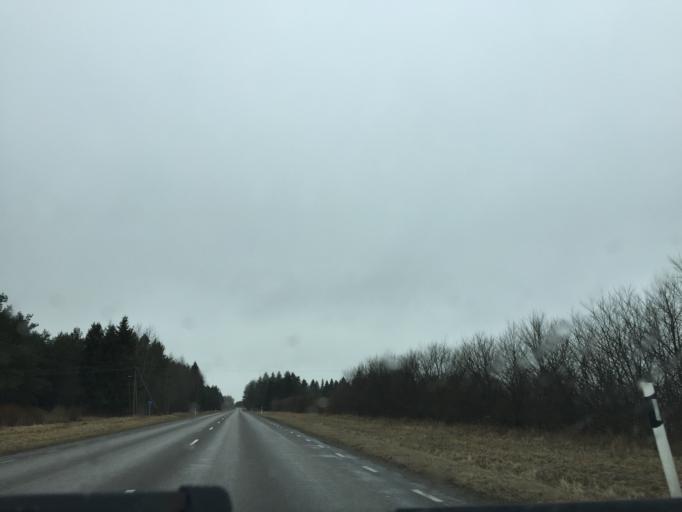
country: EE
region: Laeaene
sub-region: Ridala Parish
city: Uuemoisa
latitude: 58.8715
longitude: 23.6169
